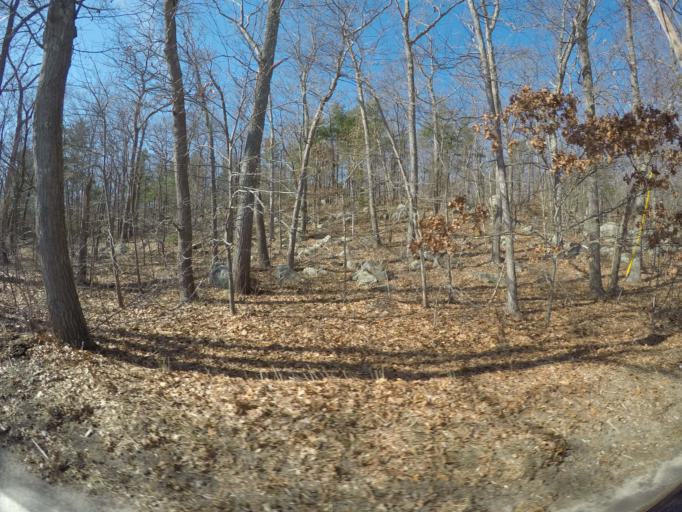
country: US
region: Massachusetts
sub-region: Norfolk County
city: Stoughton
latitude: 42.0815
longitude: -71.1181
